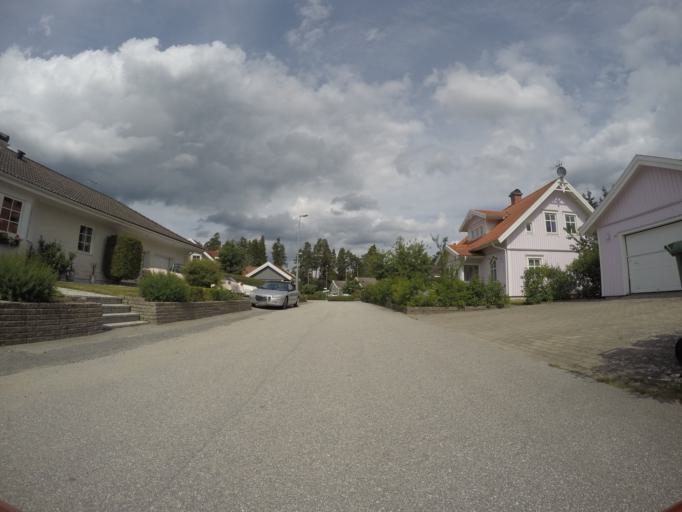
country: SE
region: Vaestra Goetaland
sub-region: Trollhattan
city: Trollhattan
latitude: 58.2311
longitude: 12.3134
